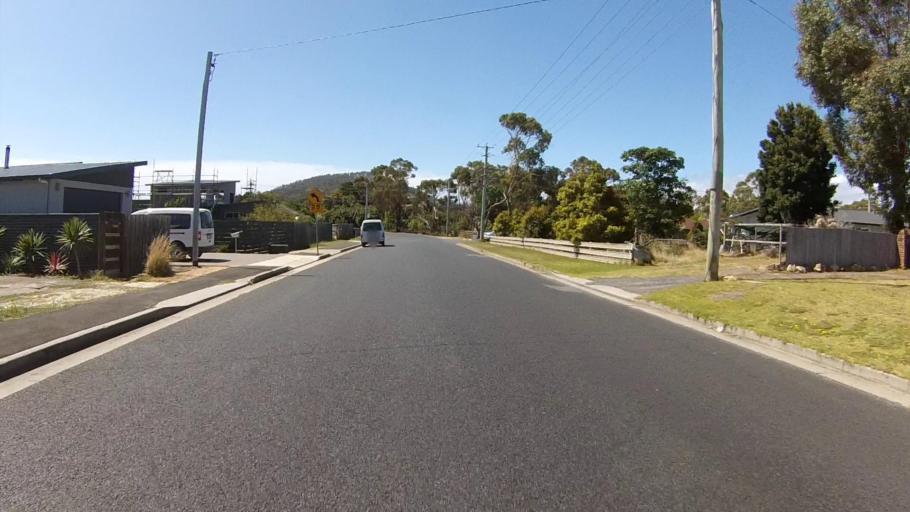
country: AU
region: Tasmania
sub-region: Clarence
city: Acton Park
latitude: -42.8949
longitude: 147.4973
